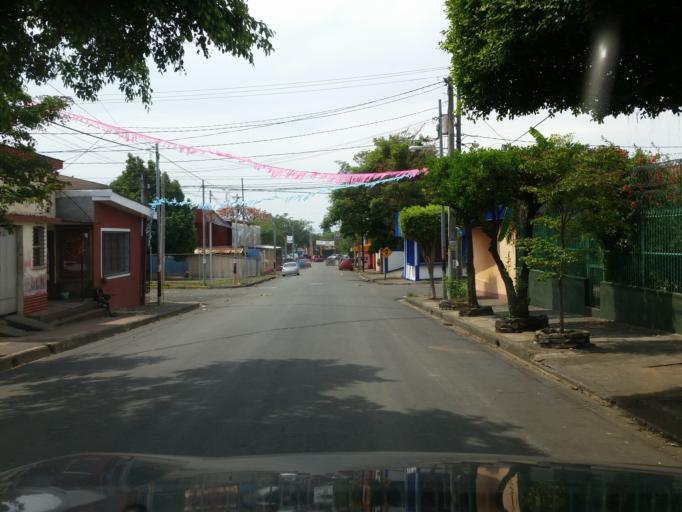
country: NI
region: Managua
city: Managua
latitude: 12.1421
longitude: -86.2914
